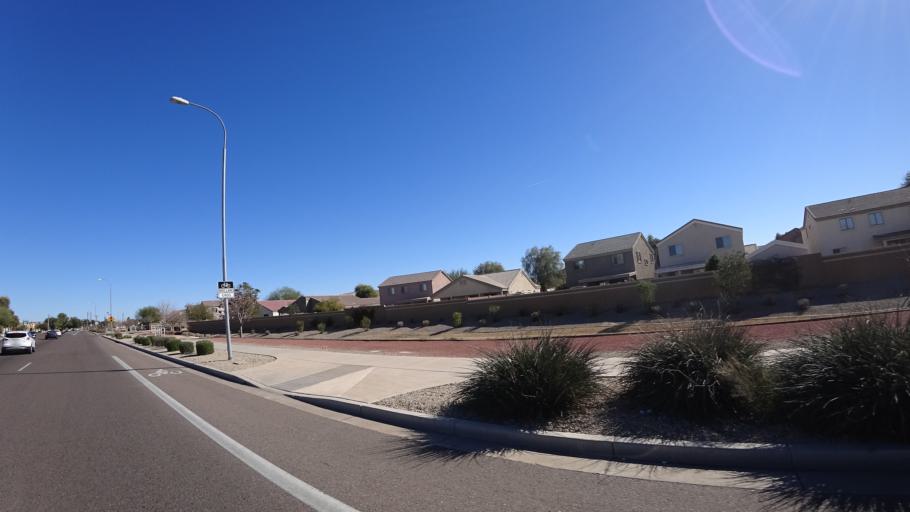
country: US
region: Arizona
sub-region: Maricopa County
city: Tolleson
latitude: 33.4226
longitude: -112.2417
